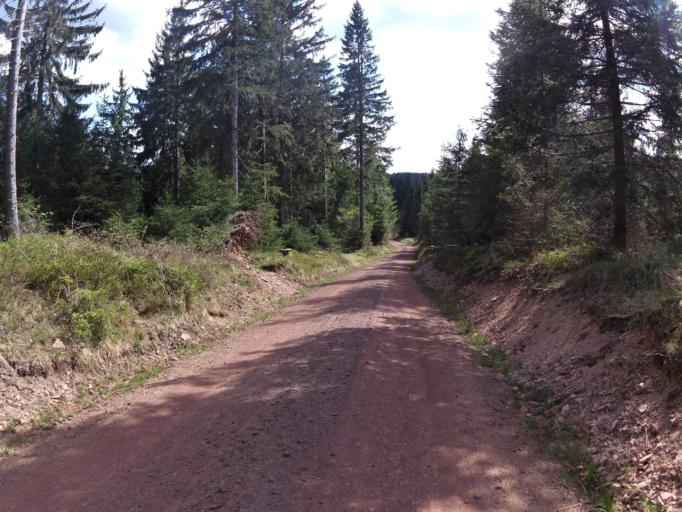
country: DE
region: Thuringia
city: Unterschonau
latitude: 50.7631
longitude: 10.5634
